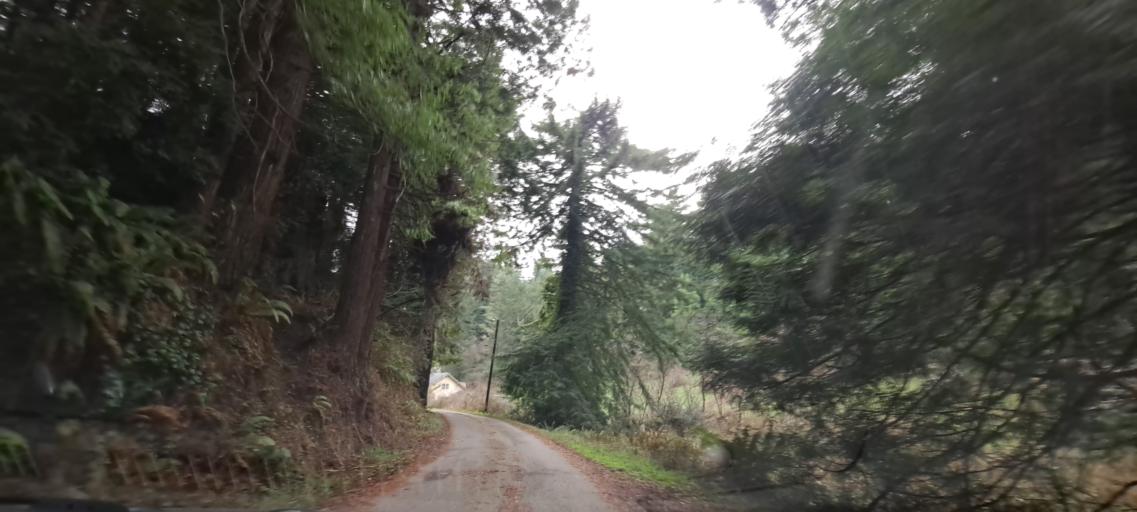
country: US
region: California
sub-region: Humboldt County
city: Fortuna
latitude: 40.6064
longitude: -124.1586
